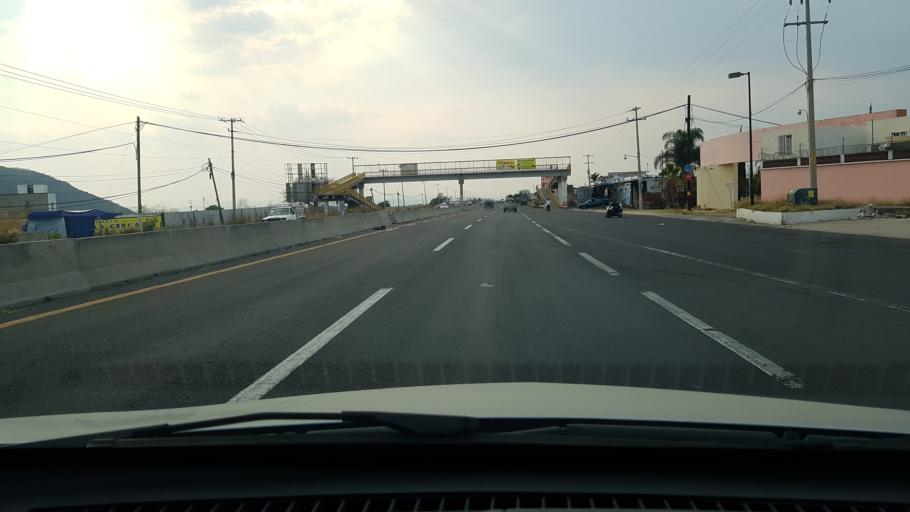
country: MX
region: Morelos
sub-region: Ayala
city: Unidad Habitacional Mariano Matamoros
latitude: 18.7511
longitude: -98.8521
